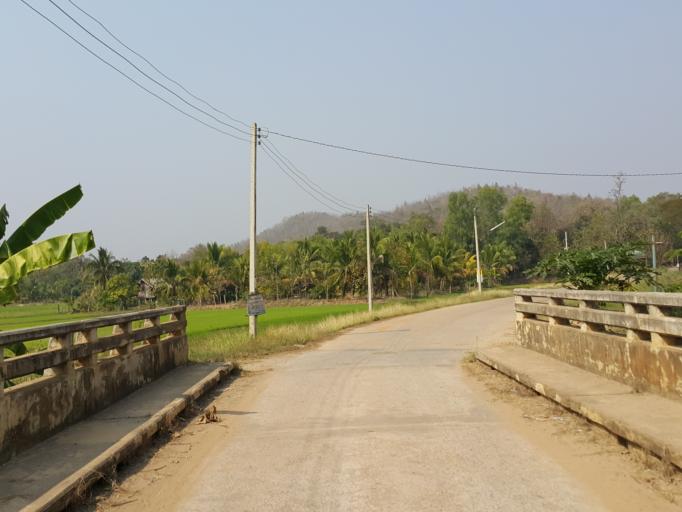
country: TH
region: Sukhothai
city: Thung Saliam
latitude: 17.3290
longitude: 99.5347
